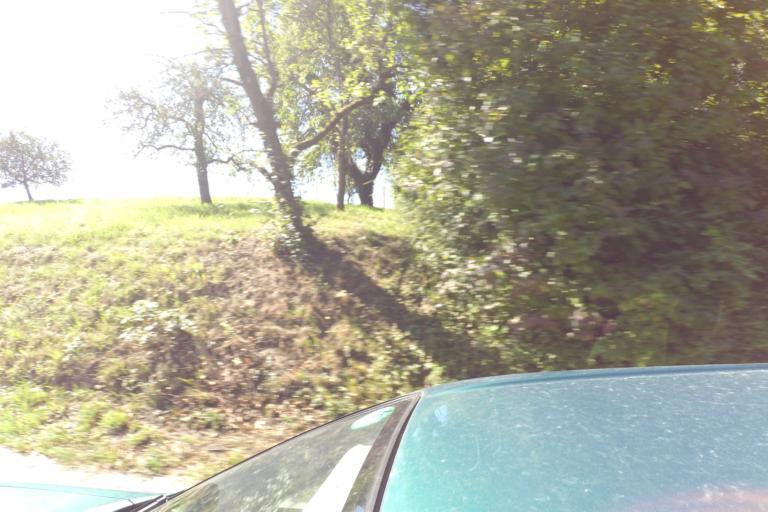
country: DE
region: Baden-Wuerttemberg
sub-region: Regierungsbezirk Stuttgart
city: Bretzfeld
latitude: 49.2358
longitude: 9.4412
